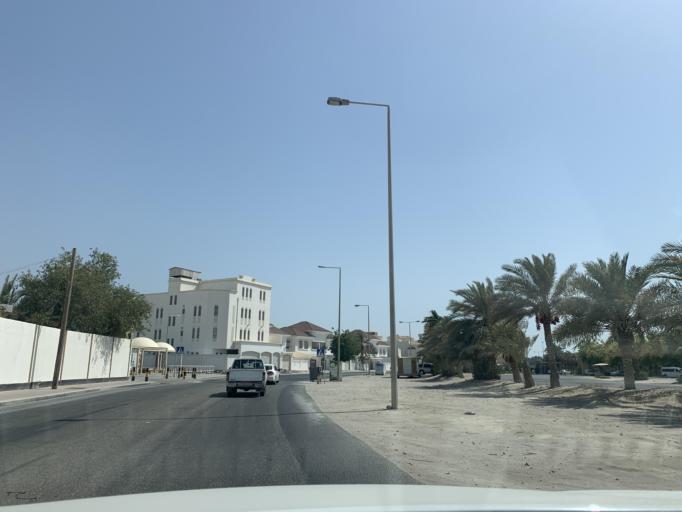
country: BH
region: Manama
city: Jidd Hafs
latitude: 26.2242
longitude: 50.4617
